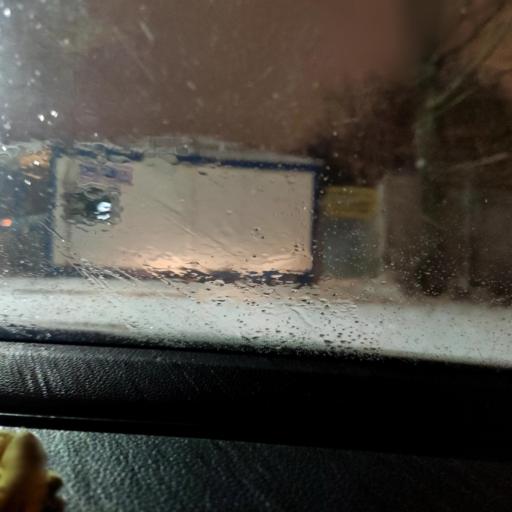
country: RU
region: Moscow
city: Mikhalkovo
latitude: 55.7019
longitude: 37.4365
